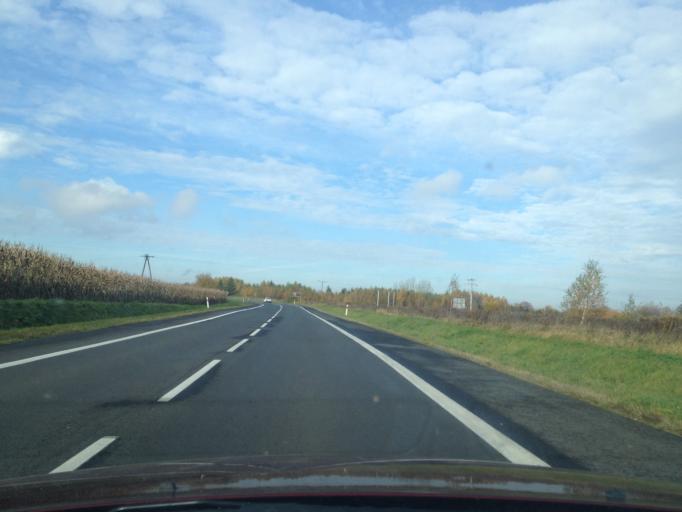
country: PL
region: Lower Silesian Voivodeship
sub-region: Powiat lubanski
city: Pisarzowice
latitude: 51.1406
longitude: 15.2325
